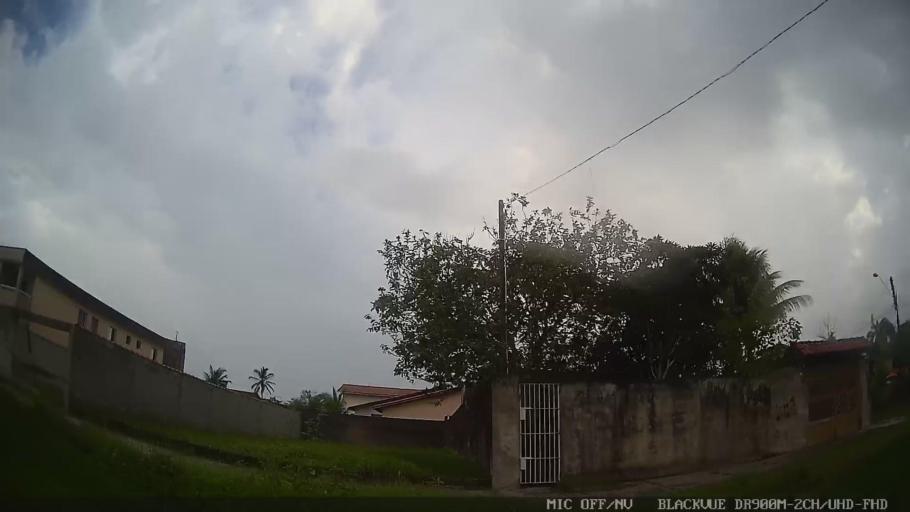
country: BR
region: Sao Paulo
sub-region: Itanhaem
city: Itanhaem
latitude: -24.2122
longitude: -46.8609
